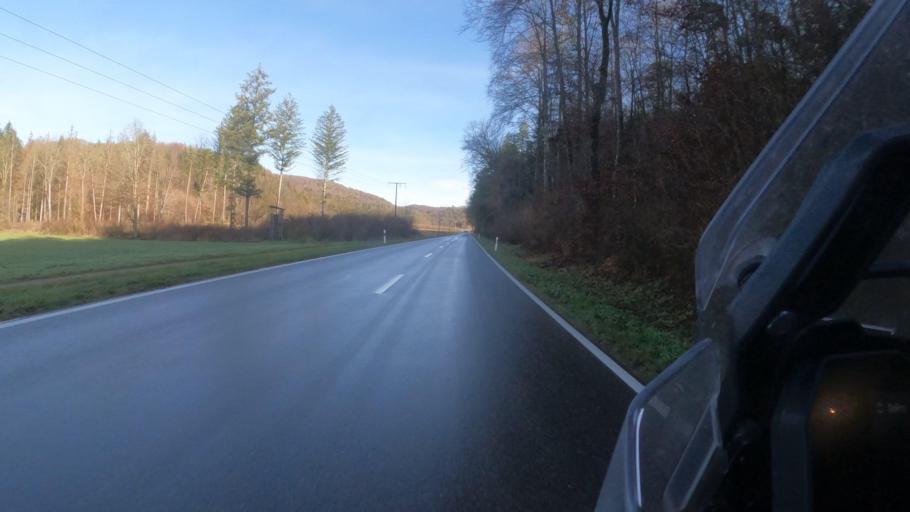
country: DE
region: Baden-Wuerttemberg
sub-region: Freiburg Region
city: Aach
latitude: 47.8450
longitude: 8.8210
